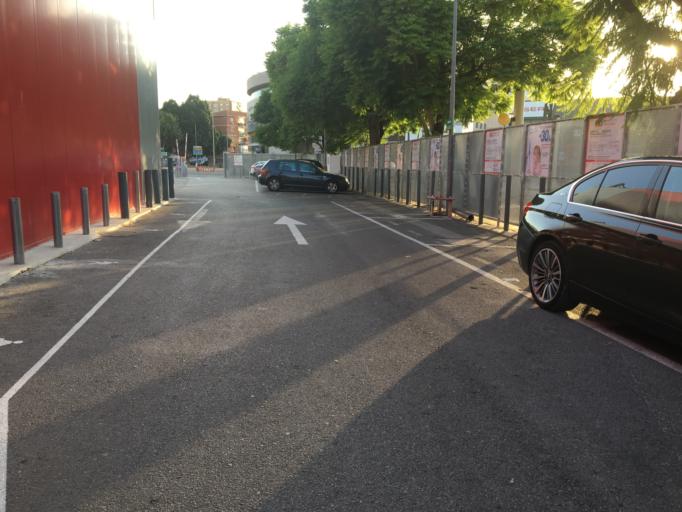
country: ES
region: Murcia
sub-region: Murcia
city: Murcia
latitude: 37.9907
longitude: -1.1164
